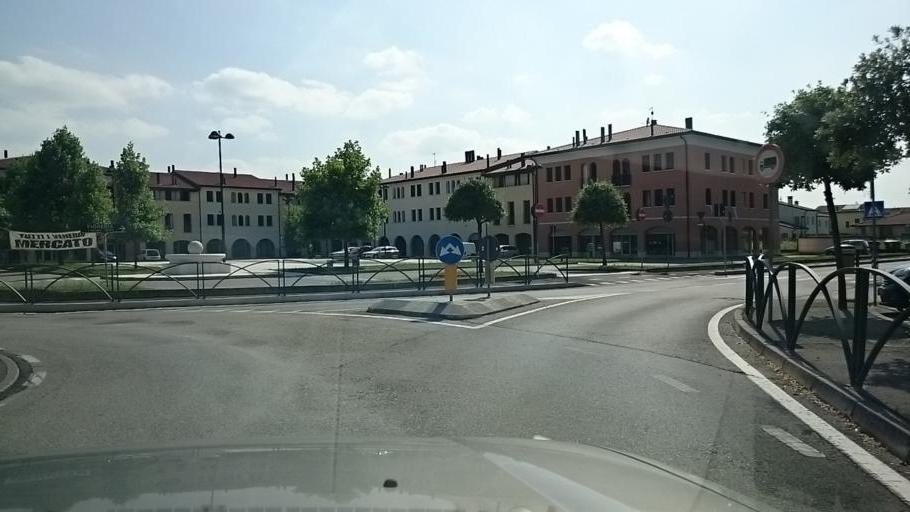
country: IT
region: Veneto
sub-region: Provincia di Padova
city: Abbazia Pisani
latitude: 45.6165
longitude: 11.8531
